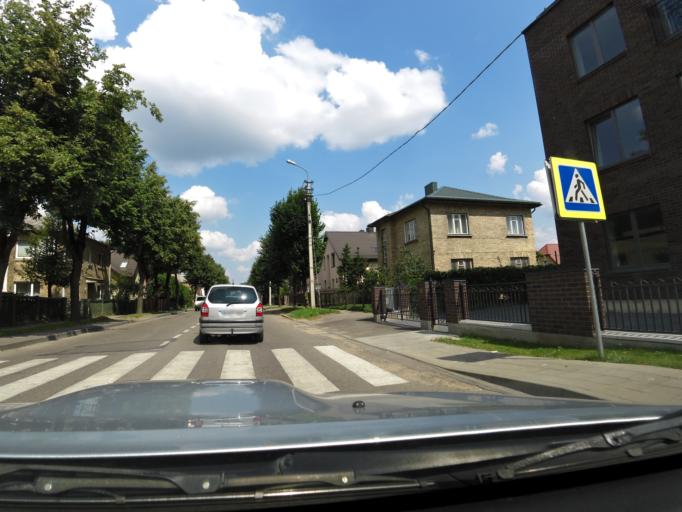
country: LT
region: Siauliu apskritis
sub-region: Siauliai
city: Siauliai
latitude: 55.9372
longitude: 23.3192
